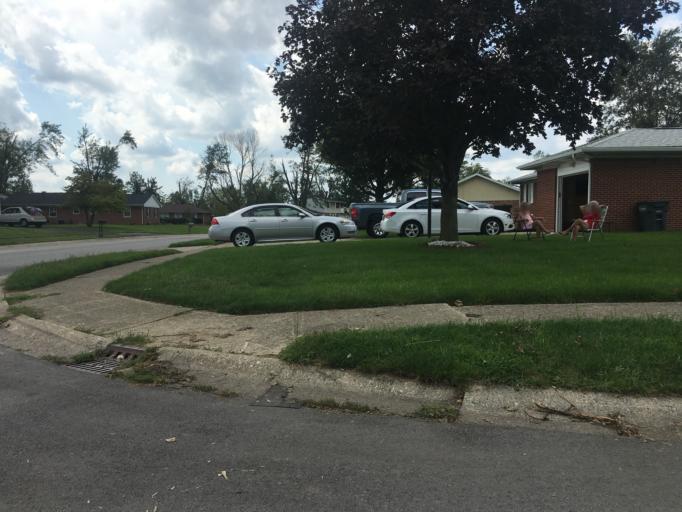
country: US
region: Indiana
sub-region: Howard County
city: Kokomo
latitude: 40.4701
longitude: -86.0998
